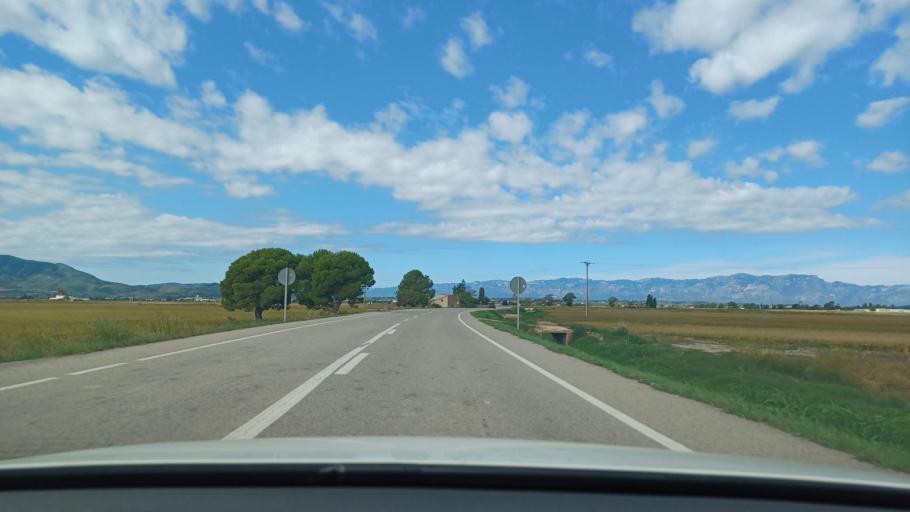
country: ES
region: Catalonia
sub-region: Provincia de Tarragona
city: Deltebre
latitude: 40.7046
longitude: 0.6497
